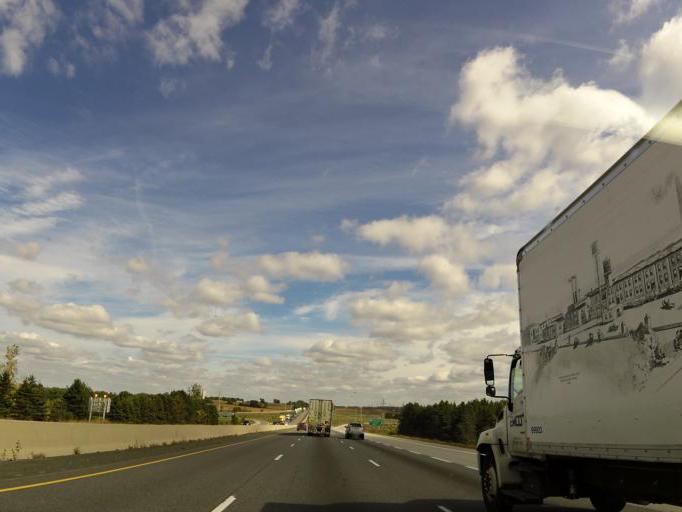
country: CA
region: Ontario
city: Ingersoll
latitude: 42.9747
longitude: -80.9578
